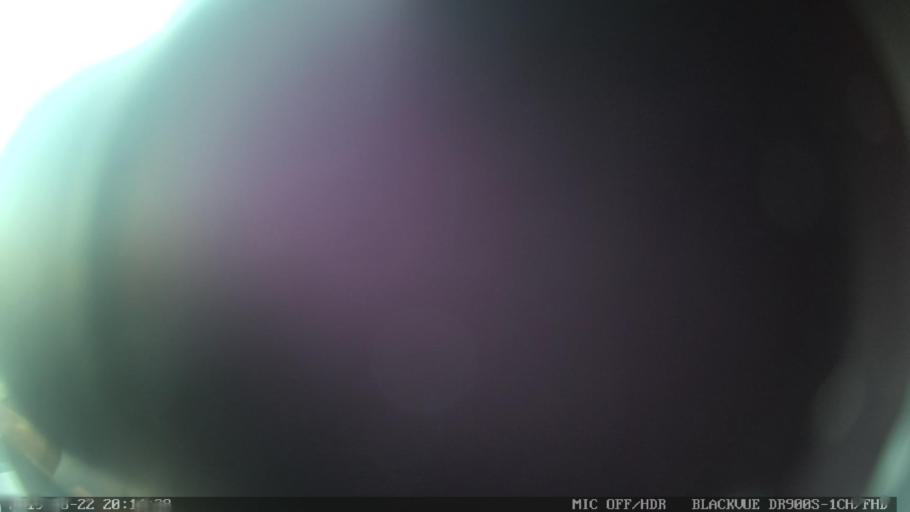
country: PT
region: Guarda
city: Alcains
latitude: 39.9221
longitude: -7.4275
